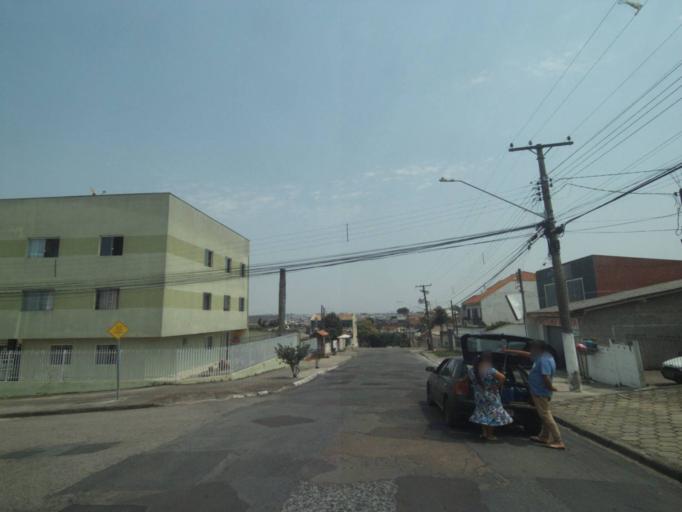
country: BR
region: Parana
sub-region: Sao Jose Dos Pinhais
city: Sao Jose dos Pinhais
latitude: -25.5390
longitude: -49.2441
